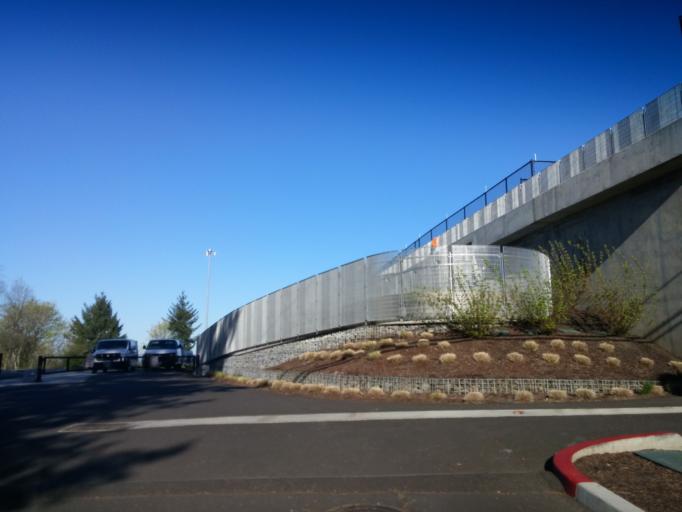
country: US
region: Oregon
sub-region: Washington County
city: West Haven-Sylvan
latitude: 45.5047
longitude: -122.7798
